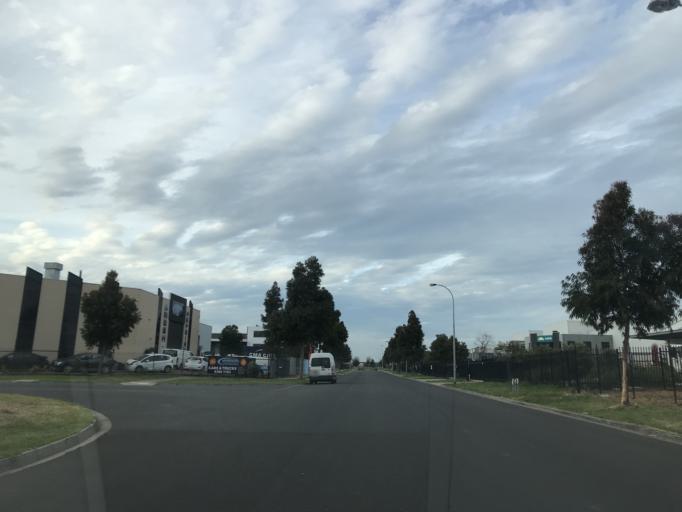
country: AU
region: Victoria
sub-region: Brimbank
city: Derrimut
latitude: -37.8038
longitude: 144.7629
